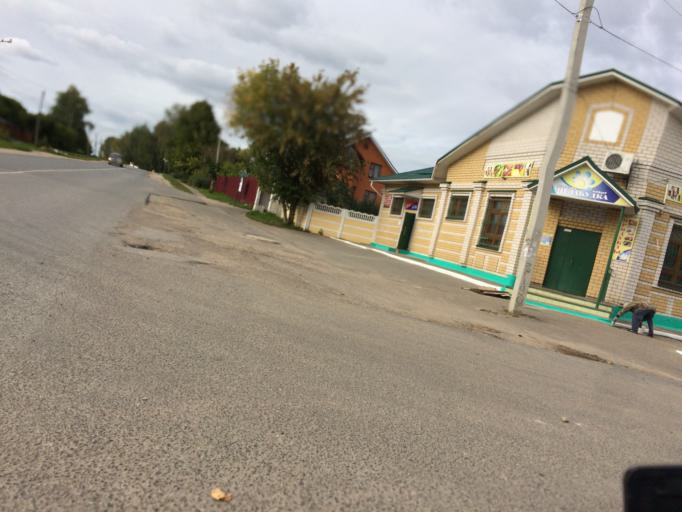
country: RU
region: Mariy-El
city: Yoshkar-Ola
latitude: 56.6508
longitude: 47.9800
